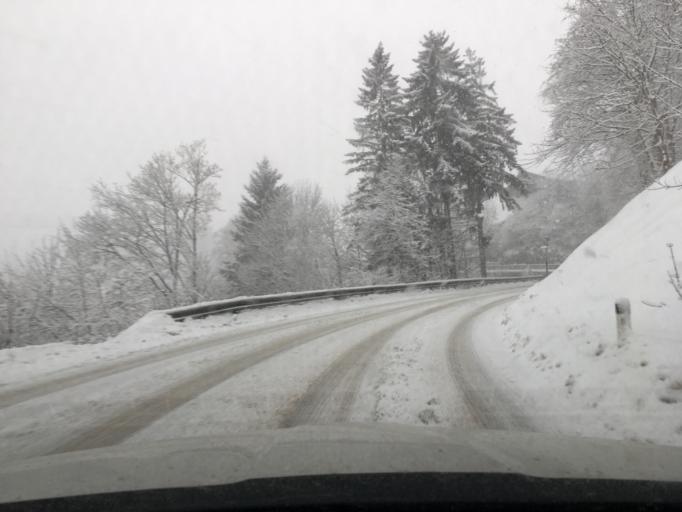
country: AT
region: Tyrol
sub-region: Politischer Bezirk Schwaz
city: Mayrhofen
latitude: 47.1574
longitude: 11.8309
